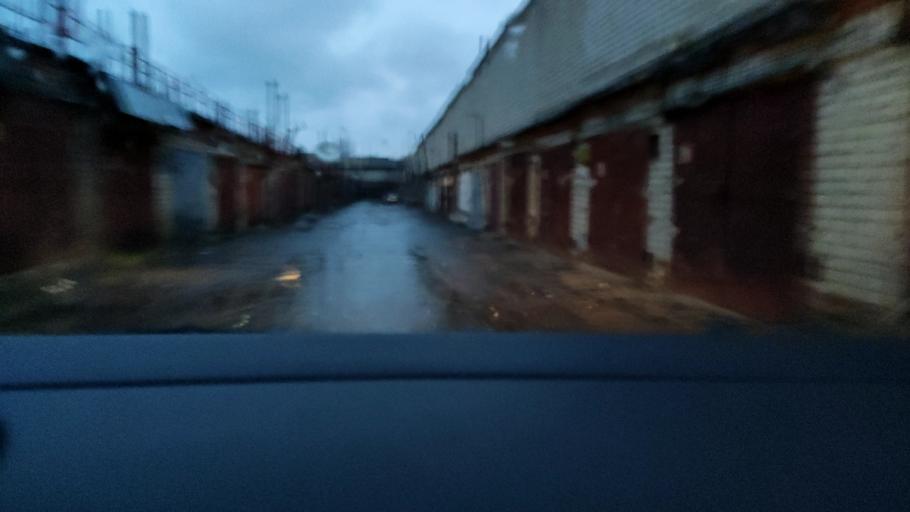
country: RU
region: Voronezj
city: Voronezh
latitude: 51.6374
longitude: 39.1552
